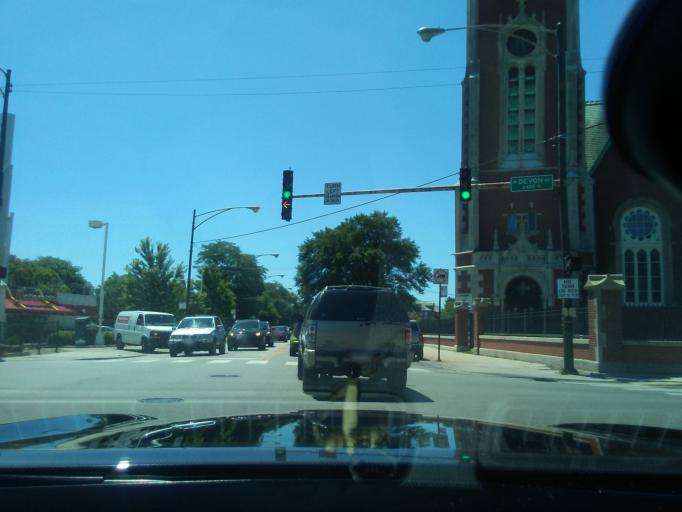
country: US
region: Illinois
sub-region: Cook County
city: Evanston
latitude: 41.9980
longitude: -87.6769
